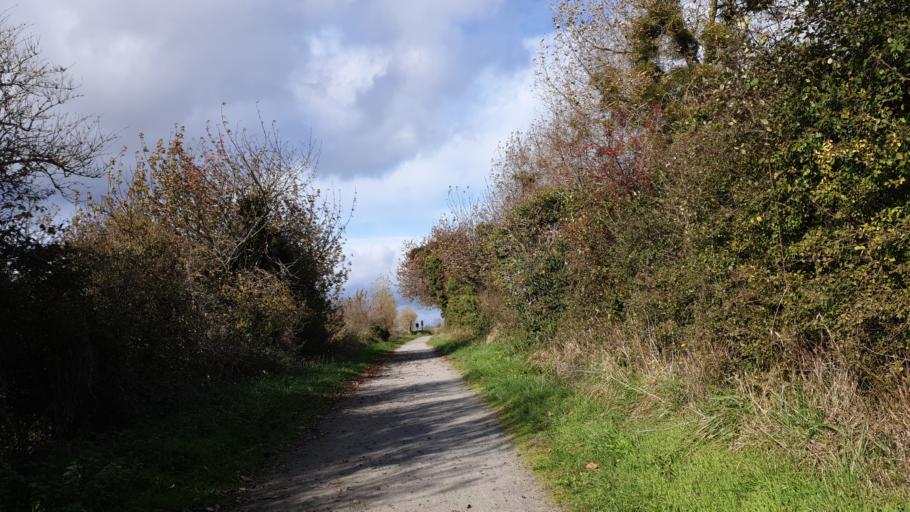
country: FR
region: Brittany
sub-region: Departement d'Ille-et-Vilaine
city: Saint-Broladre
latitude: 48.6086
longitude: -1.6642
